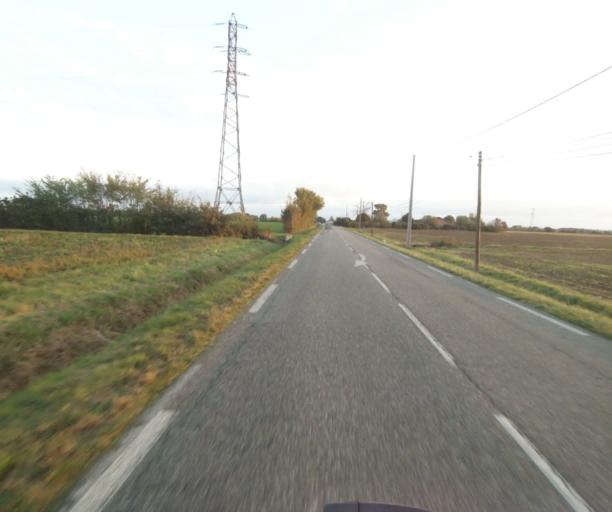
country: FR
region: Midi-Pyrenees
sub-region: Departement du Tarn-et-Garonne
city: Verdun-sur-Garonne
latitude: 43.8371
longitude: 1.2397
